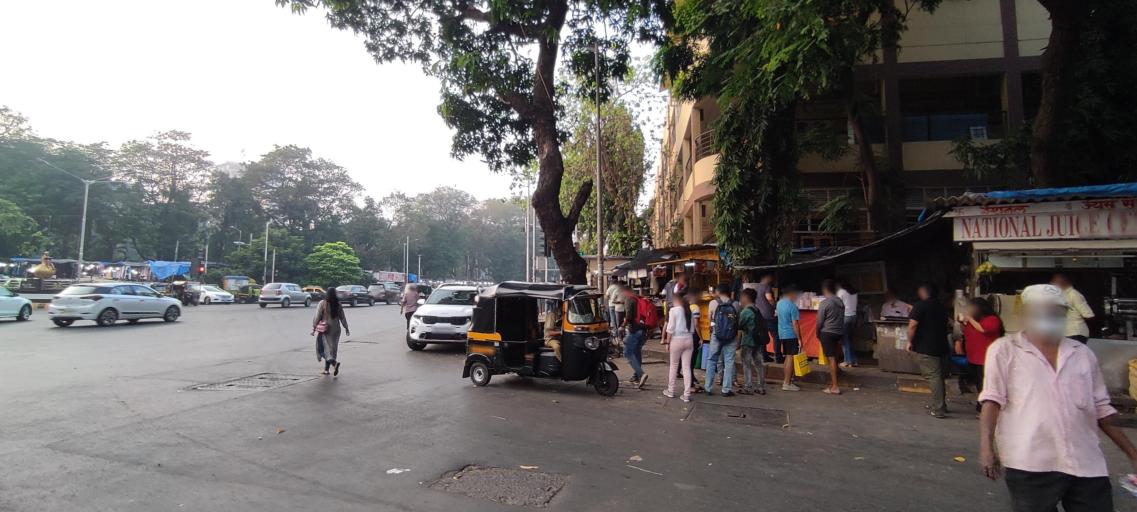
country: IN
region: Maharashtra
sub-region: Mumbai Suburban
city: Mumbai
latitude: 19.0636
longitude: 72.8353
